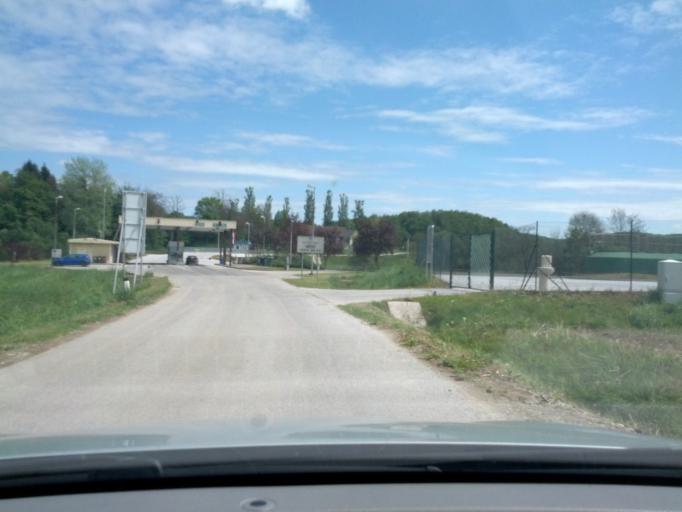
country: SI
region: Podcetrtek
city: Podcetrtek
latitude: 46.1290
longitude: 15.6095
